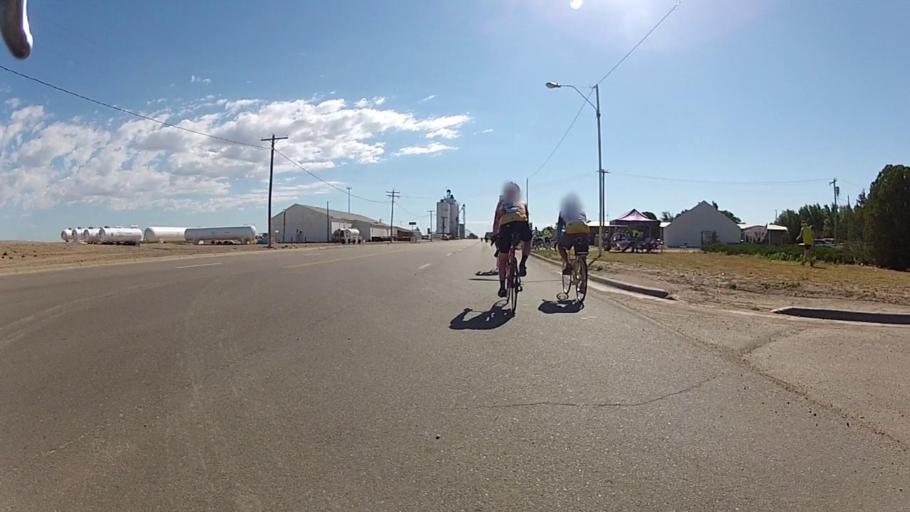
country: US
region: Kansas
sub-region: Gray County
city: Cimarron
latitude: 37.5974
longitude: -100.4486
